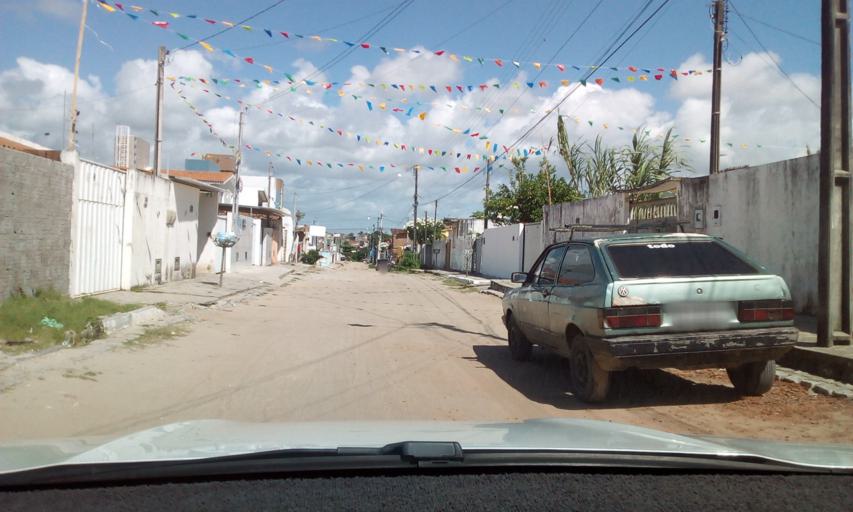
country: BR
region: Paraiba
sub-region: Joao Pessoa
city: Joao Pessoa
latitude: -7.2028
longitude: -34.8335
